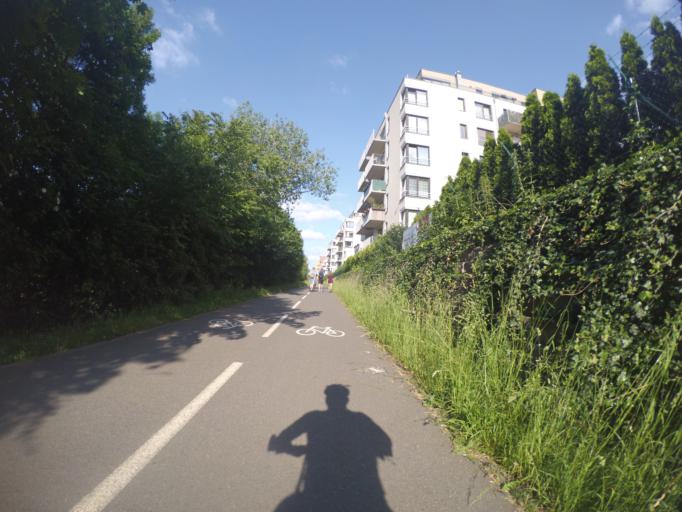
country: CZ
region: Praha
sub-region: Praha 9
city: Vysocany
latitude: 50.1054
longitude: 14.5172
